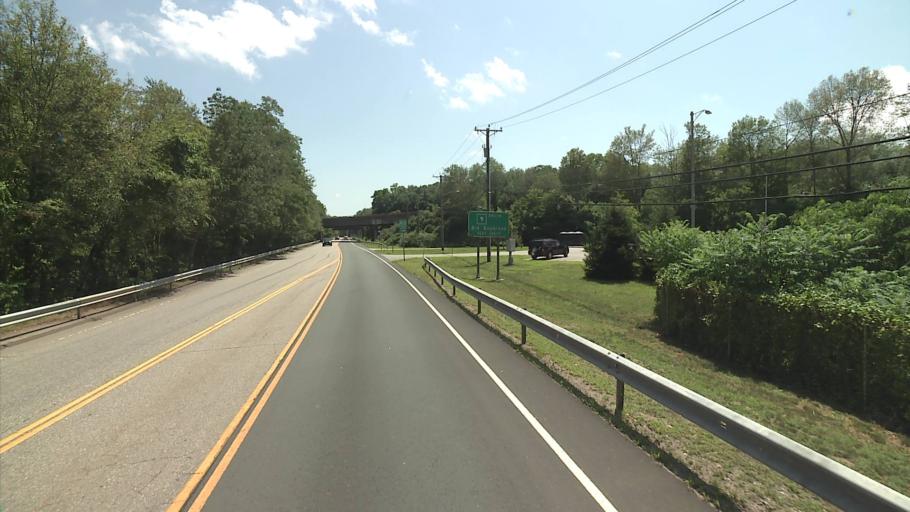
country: US
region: Connecticut
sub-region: Middlesex County
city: Deep River Center
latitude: 41.3632
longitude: -72.4242
